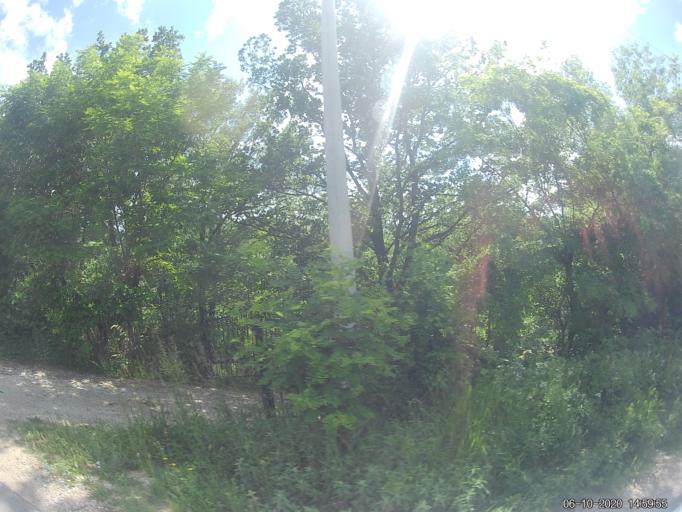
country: XK
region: Ferizaj
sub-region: Komuna e Shtimes
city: Shtime
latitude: 42.4131
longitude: 21.0278
